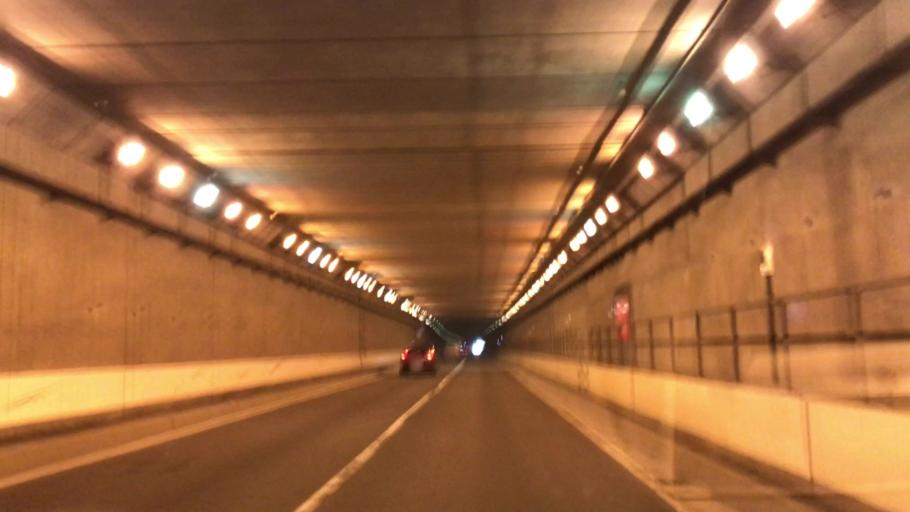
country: JP
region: Hokkaido
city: Sapporo
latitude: 43.0629
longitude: 141.3567
